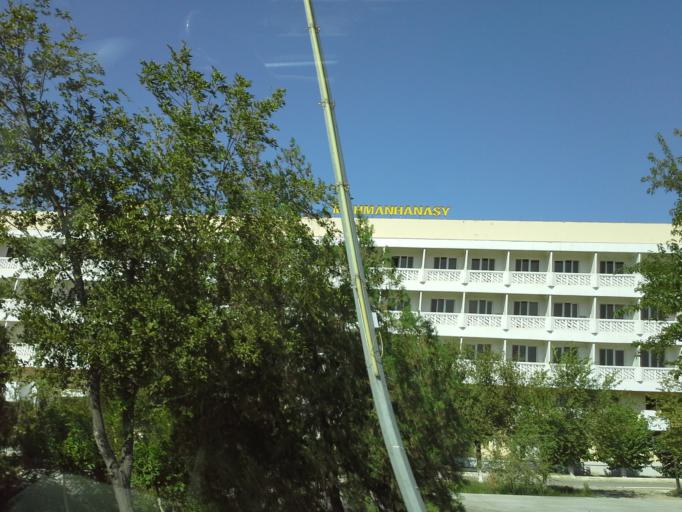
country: TM
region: Dasoguz
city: Dasoguz
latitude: 41.8339
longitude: 59.9683
